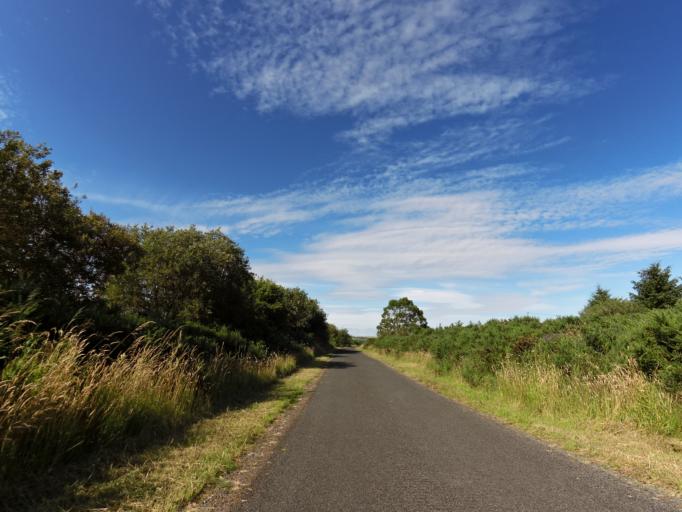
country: IE
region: Munster
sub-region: Waterford
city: Portlaw
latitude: 52.2155
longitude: -7.3555
